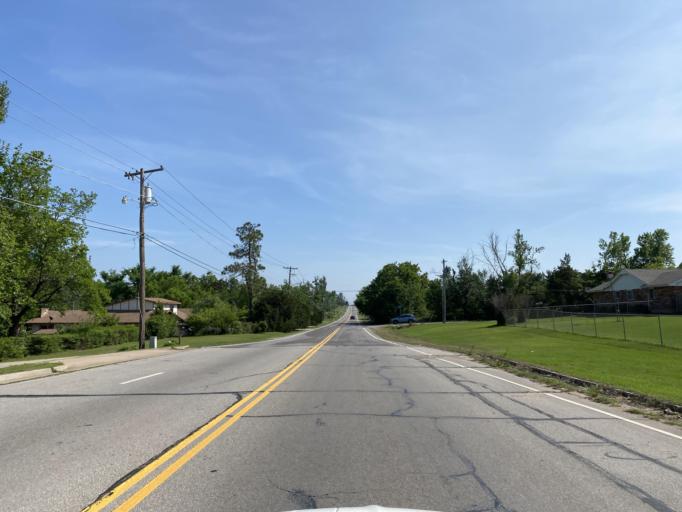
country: US
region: Oklahoma
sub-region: Oklahoma County
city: Nicoma Park
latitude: 35.4628
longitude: -97.3357
